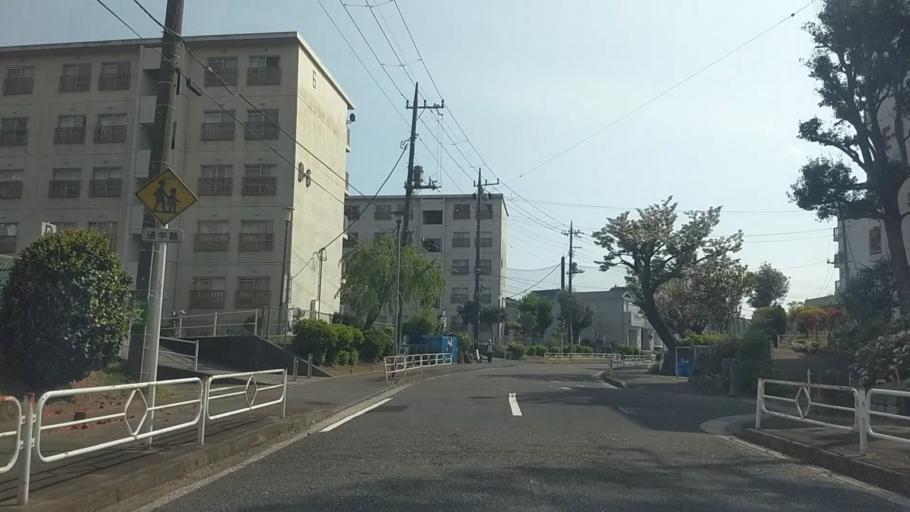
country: JP
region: Kanagawa
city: Kamakura
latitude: 35.3839
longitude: 139.5703
